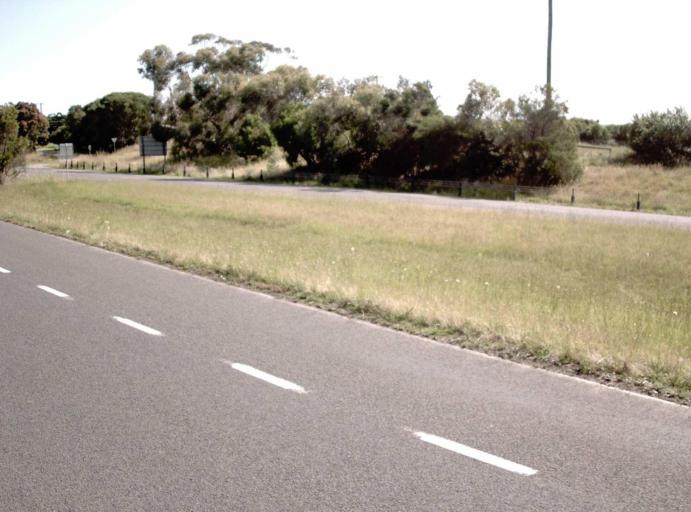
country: AU
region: Victoria
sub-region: Cardinia
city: Koo-Wee-Rup
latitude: -38.2836
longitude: 145.5471
